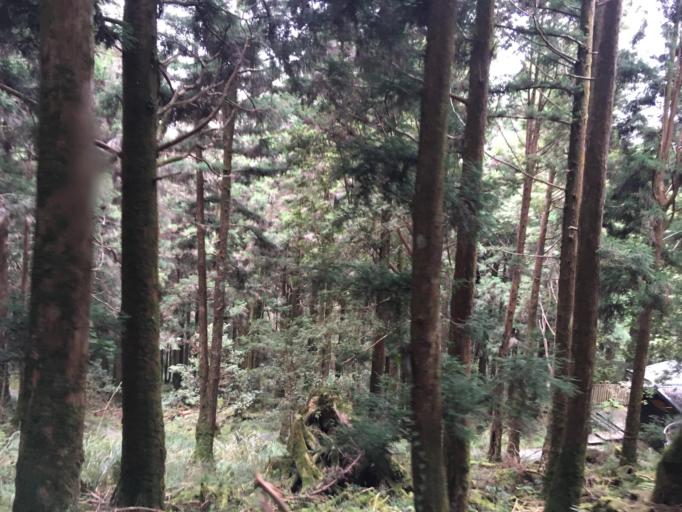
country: TW
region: Taiwan
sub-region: Yilan
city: Yilan
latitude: 24.4788
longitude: 121.5364
